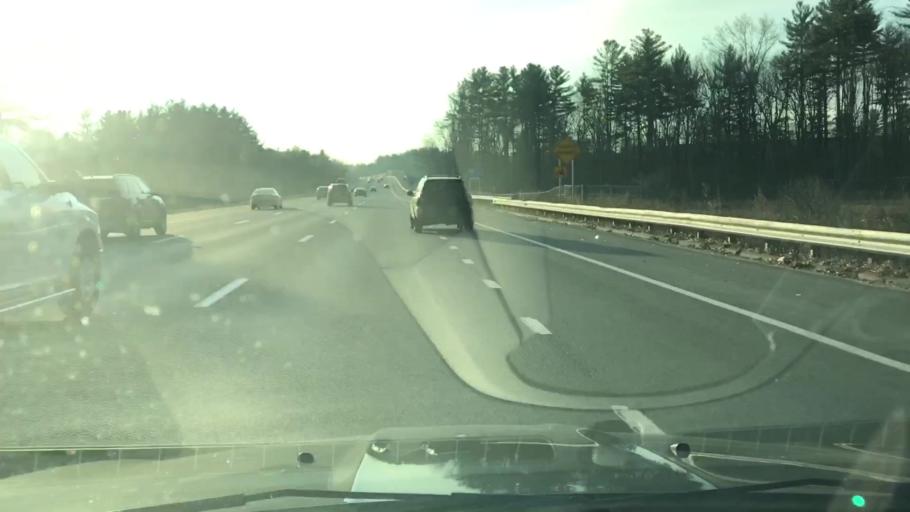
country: US
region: New Hampshire
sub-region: Rockingham County
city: Salem
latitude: 42.7706
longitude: -71.2411
